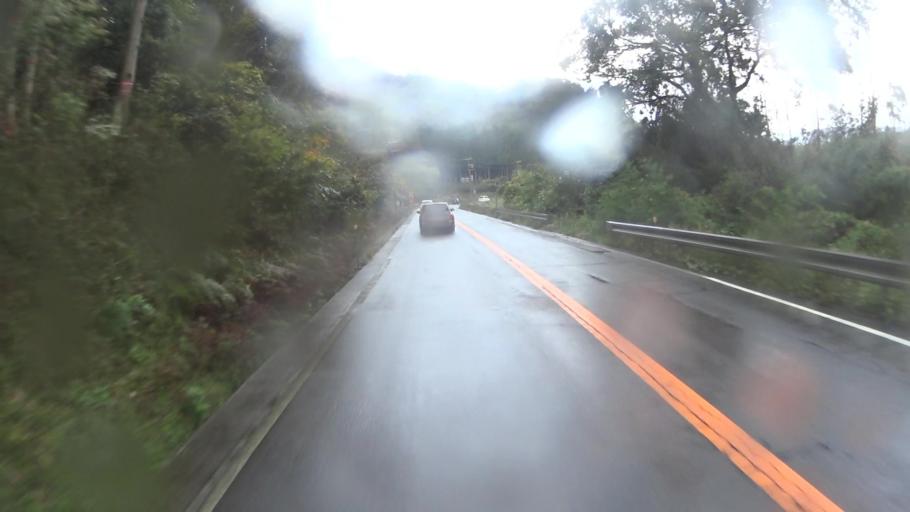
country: JP
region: Kyoto
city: Ayabe
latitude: 35.1964
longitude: 135.2848
